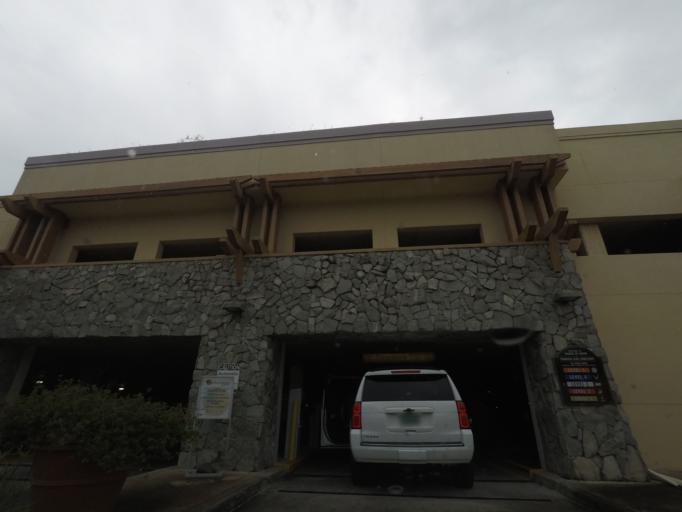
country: US
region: Florida
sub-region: Polk County
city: Citrus Ridge
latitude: 28.4020
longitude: -81.5906
